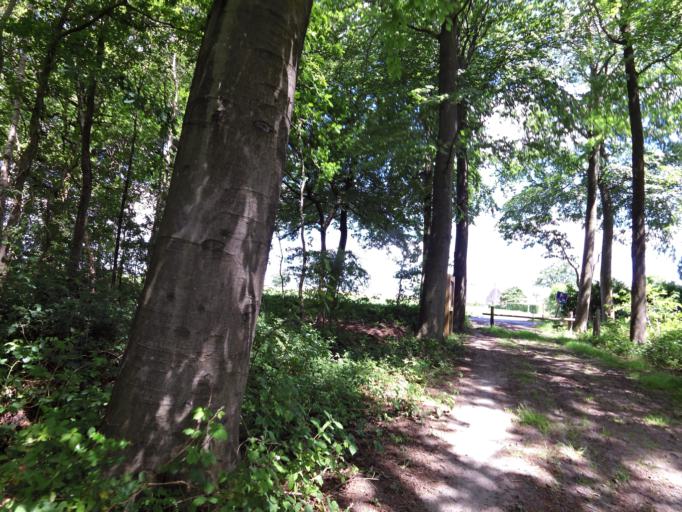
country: BE
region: Flanders
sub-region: Provincie West-Vlaanderen
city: Zedelgem
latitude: 51.1543
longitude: 3.1223
